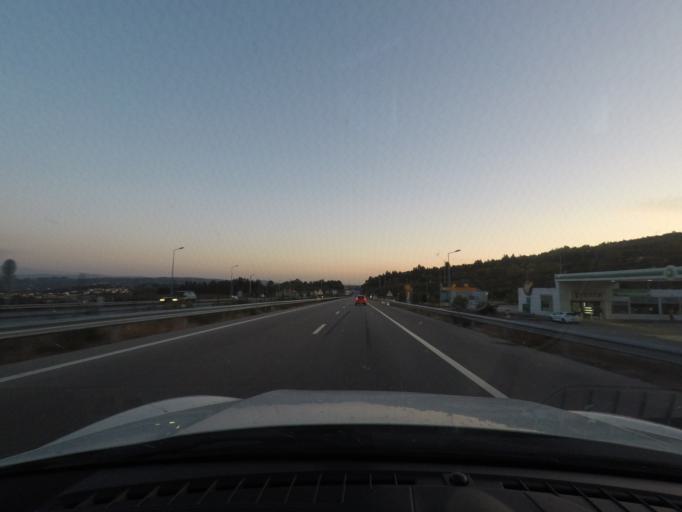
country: PT
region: Porto
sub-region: Lousada
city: Lousada
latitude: 41.3049
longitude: -8.2618
